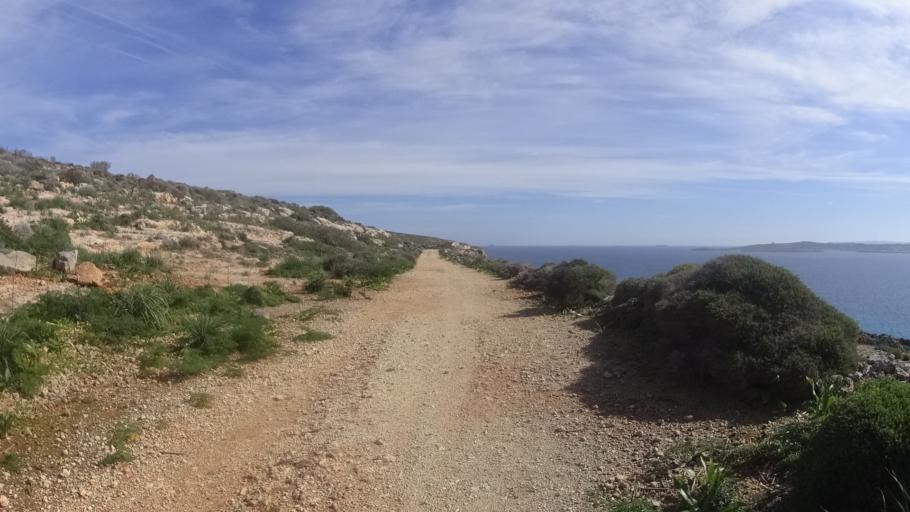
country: MT
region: Il-Qala
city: Qala
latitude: 36.0063
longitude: 14.3405
